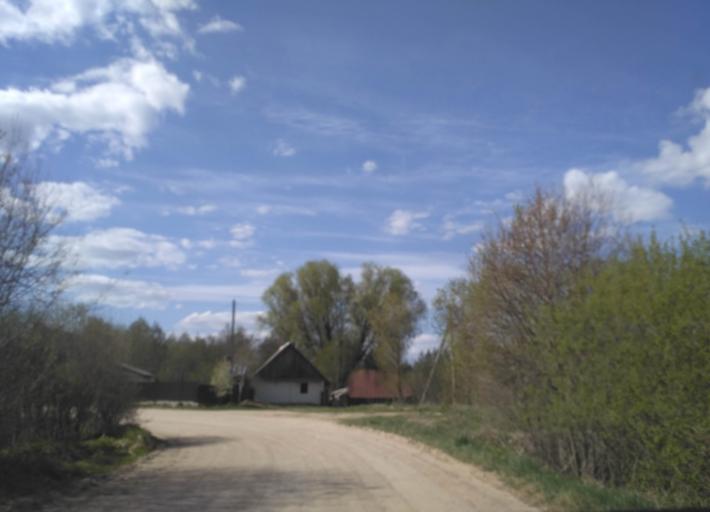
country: BY
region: Minsk
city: Narach
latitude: 54.9895
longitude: 26.5956
